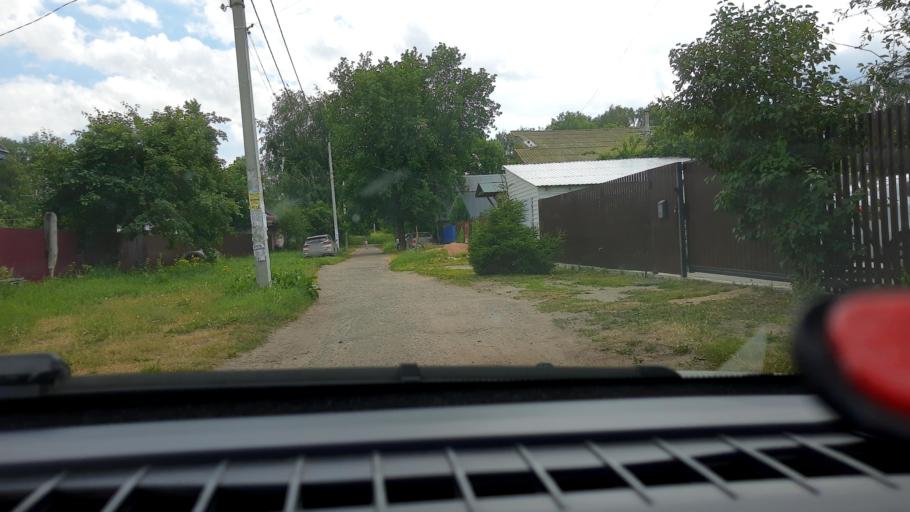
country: RU
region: Nizjnij Novgorod
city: Gorbatovka
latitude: 56.2668
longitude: 43.7563
